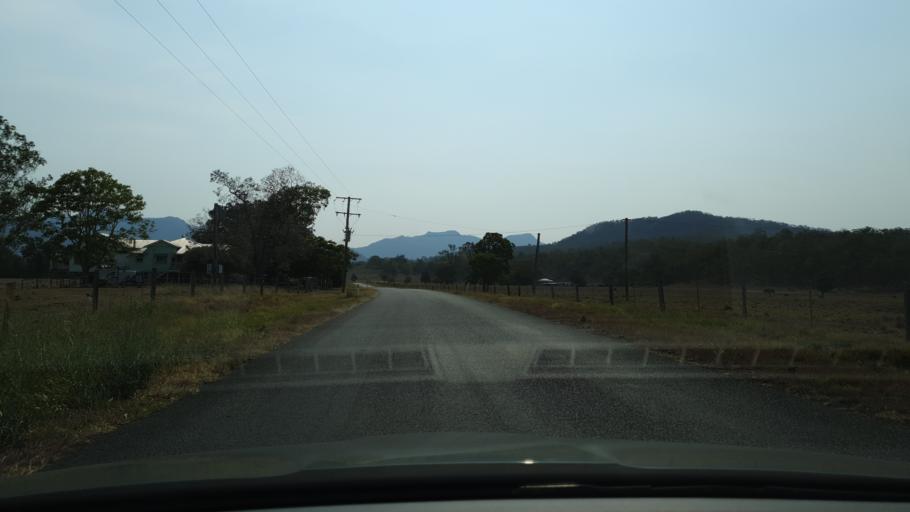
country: AU
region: Queensland
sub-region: Ipswich
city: Deebing Heights
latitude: -28.1377
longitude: 152.5786
